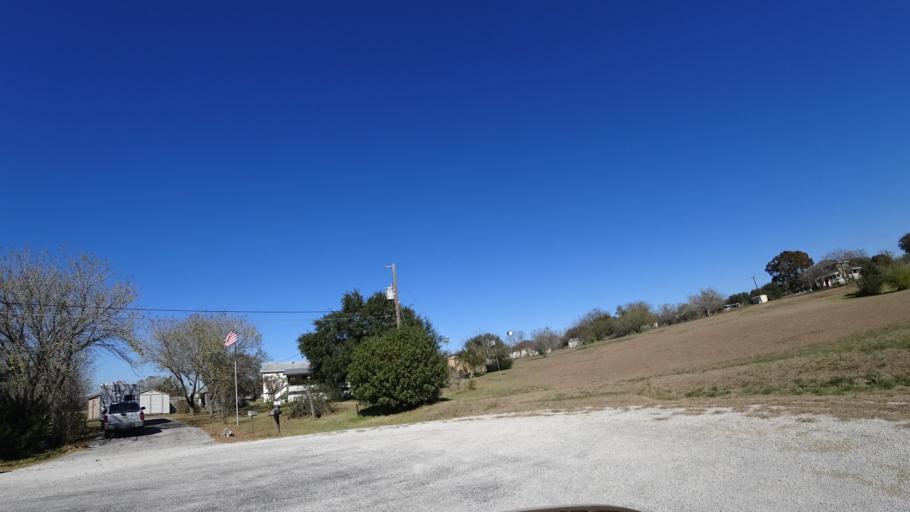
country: US
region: Texas
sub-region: Travis County
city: Garfield
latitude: 30.1041
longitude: -97.5960
